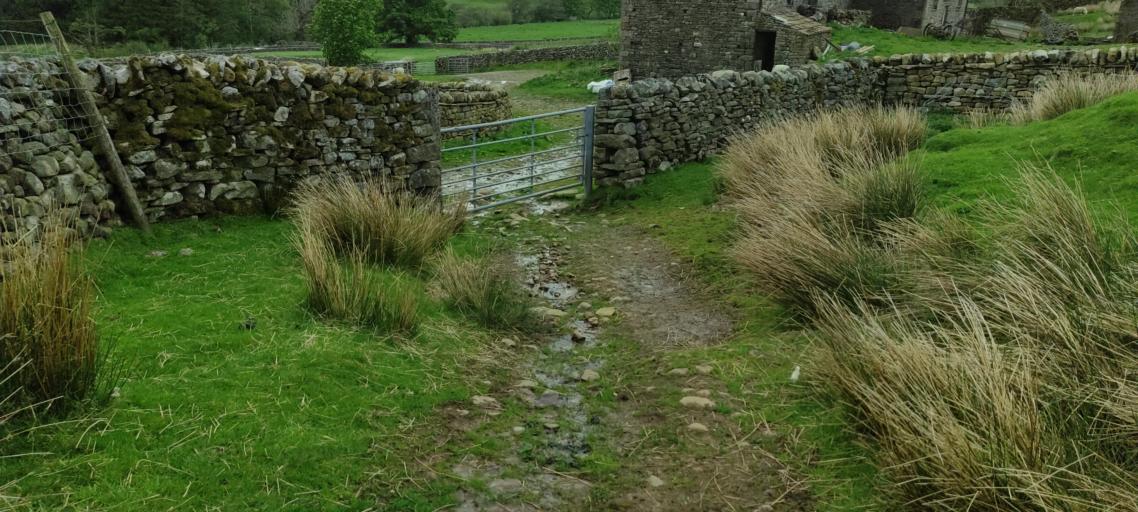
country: GB
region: England
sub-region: Cumbria
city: Kirkby Stephen
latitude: 54.3900
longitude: -2.3350
